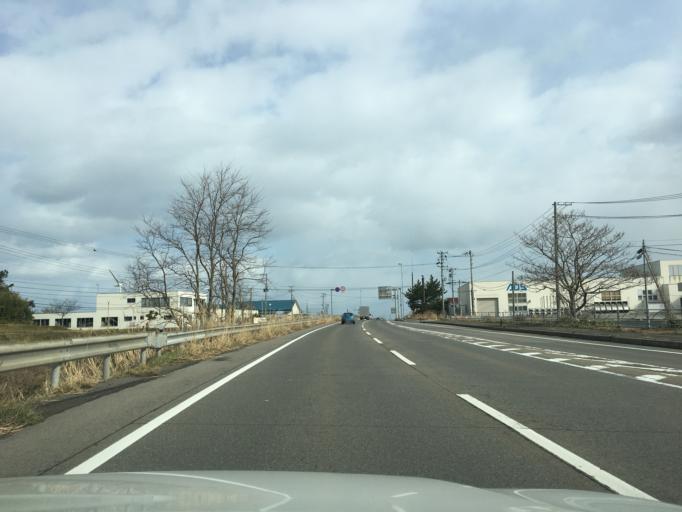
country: JP
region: Yamagata
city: Yuza
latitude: 39.2674
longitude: 139.9228
